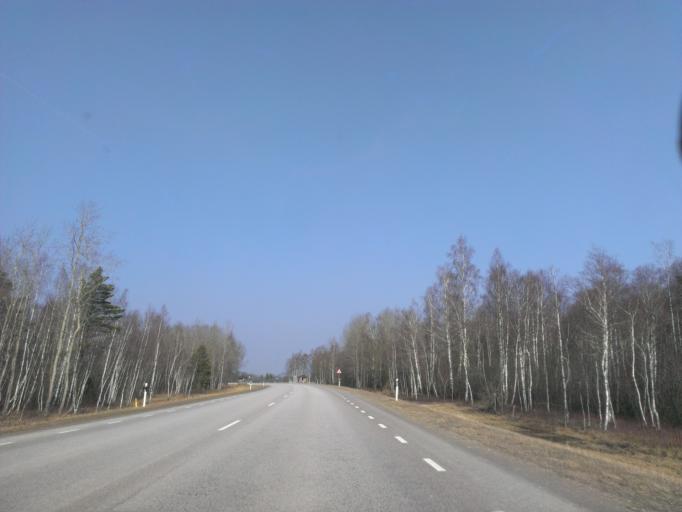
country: EE
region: Saare
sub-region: Orissaare vald
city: Orissaare
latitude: 58.4225
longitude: 22.7886
